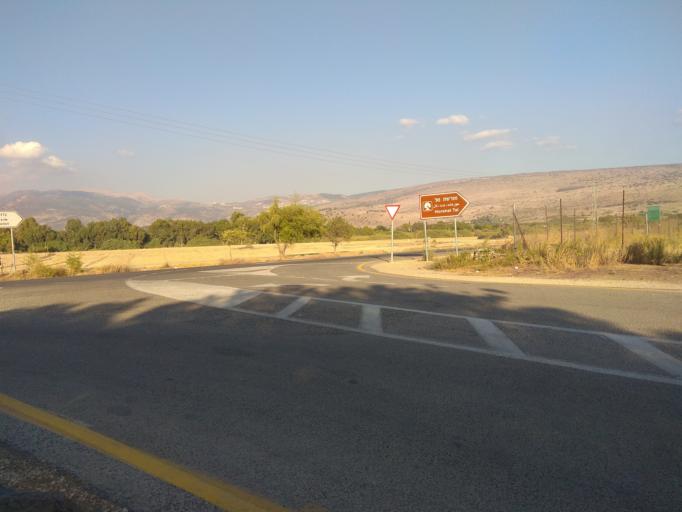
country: IL
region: Northern District
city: Qiryat Shemona
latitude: 33.2215
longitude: 35.6337
